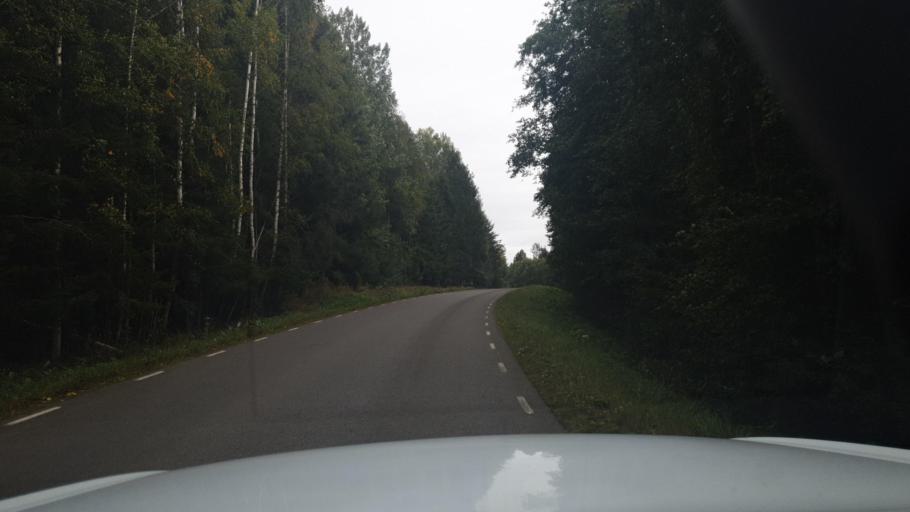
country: SE
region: Vaermland
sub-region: Torsby Kommun
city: Torsby
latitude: 60.0143
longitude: 12.6637
